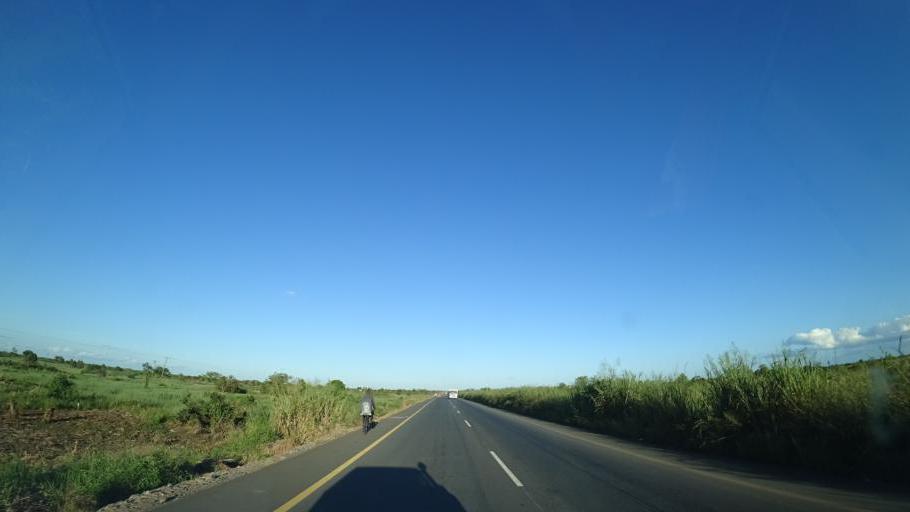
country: MZ
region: Sofala
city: Dondo
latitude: -19.3244
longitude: 34.3013
